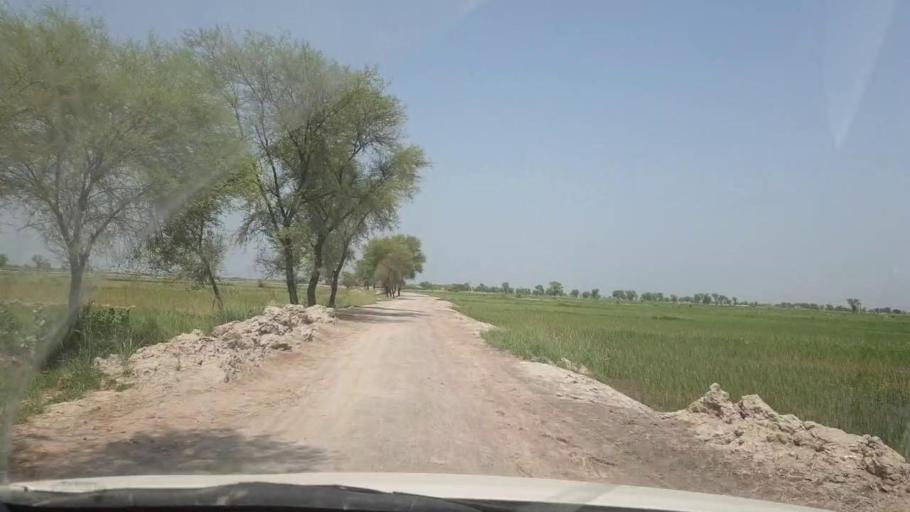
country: PK
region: Sindh
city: Lakhi
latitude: 27.8719
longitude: 68.7330
